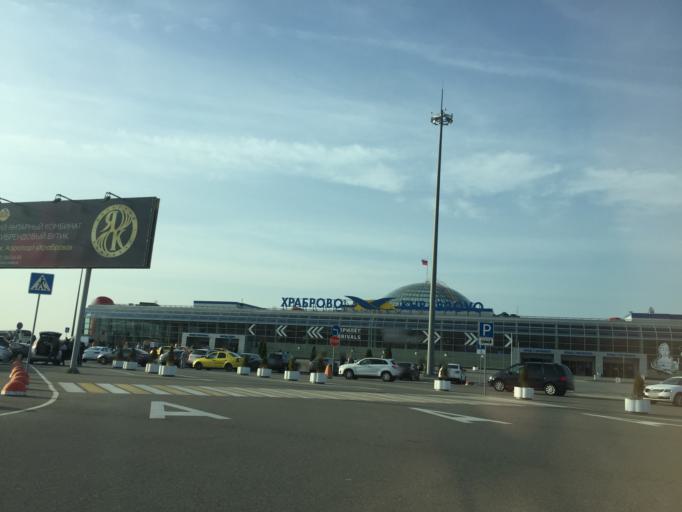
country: RU
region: Kaliningrad
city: Gur'yevsk
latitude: 54.8818
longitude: 20.5871
